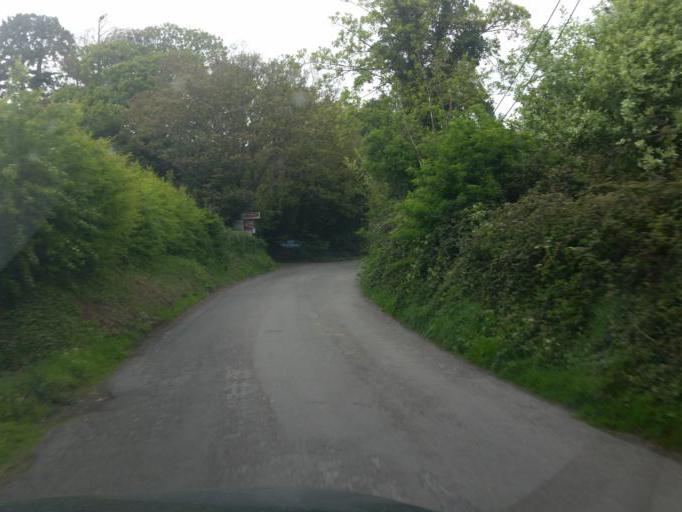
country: IE
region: Leinster
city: Castleknock
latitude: 53.3811
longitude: -6.3357
